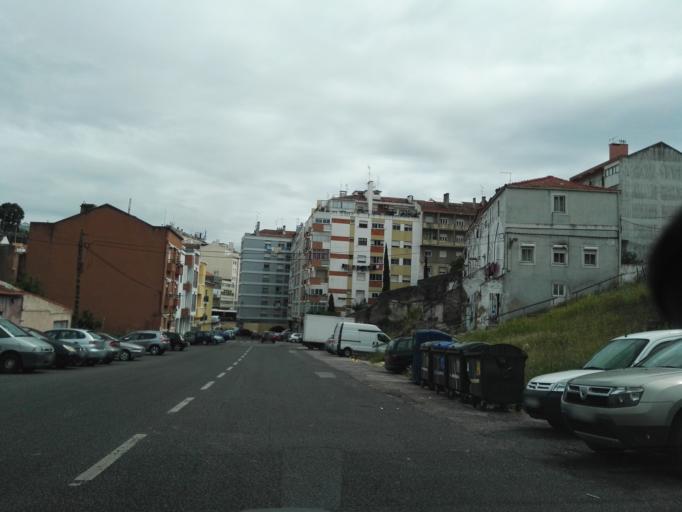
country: PT
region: Lisbon
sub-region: Oeiras
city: Alges
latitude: 38.7049
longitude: -9.1921
